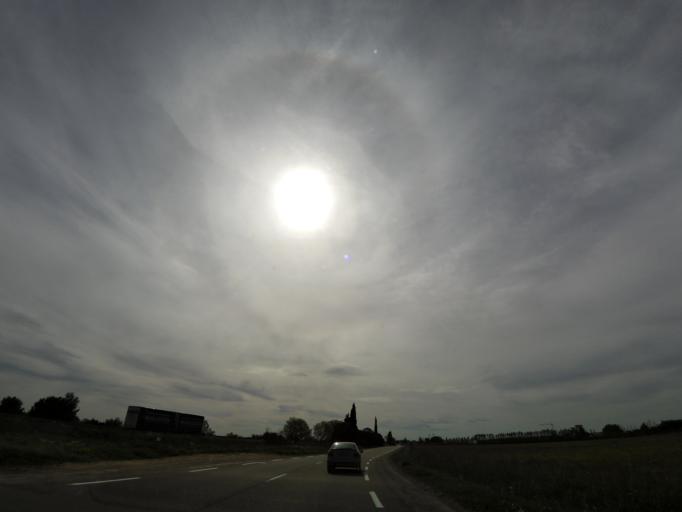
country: FR
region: Languedoc-Roussillon
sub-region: Departement du Gard
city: Gallargues-le-Montueux
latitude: 43.7127
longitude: 4.1849
